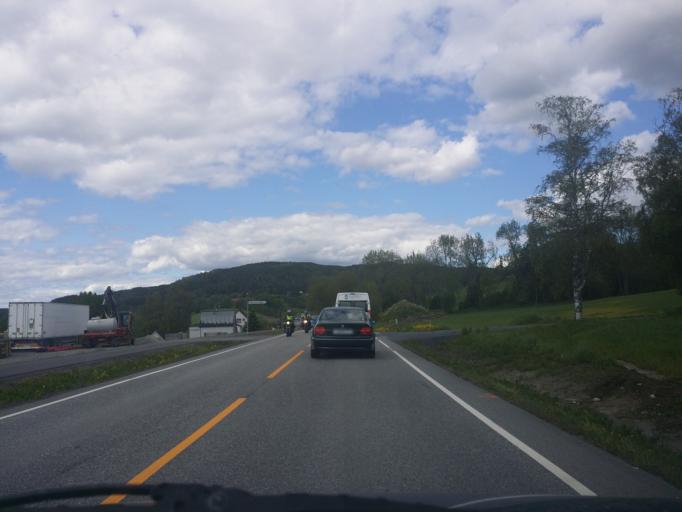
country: NO
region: Oppland
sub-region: Jevnaker
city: Jevnaker
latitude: 60.2463
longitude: 10.4247
